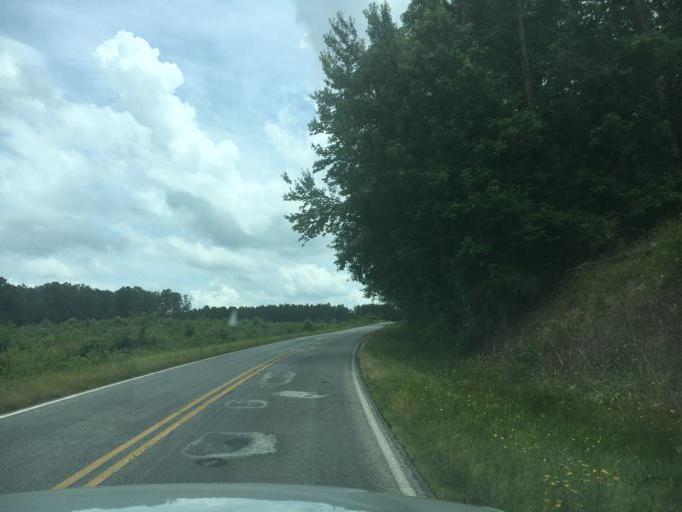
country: US
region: Georgia
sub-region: Hart County
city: Reed Creek
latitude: 34.4342
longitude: -82.9528
